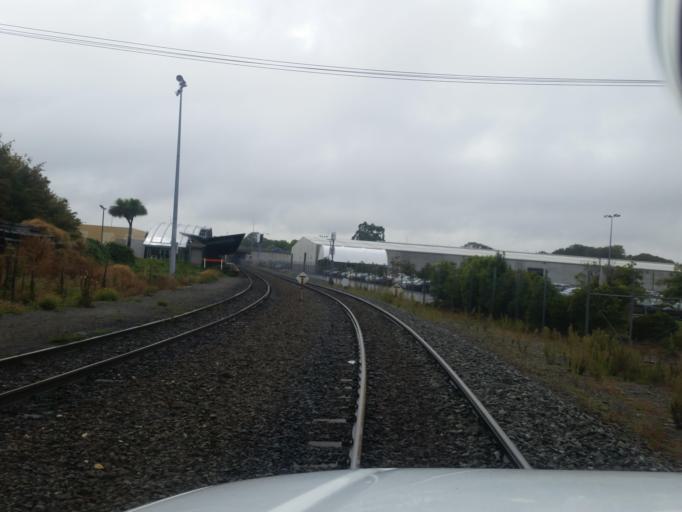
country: NZ
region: Canterbury
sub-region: Christchurch City
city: Christchurch
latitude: -43.5409
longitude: 172.6065
